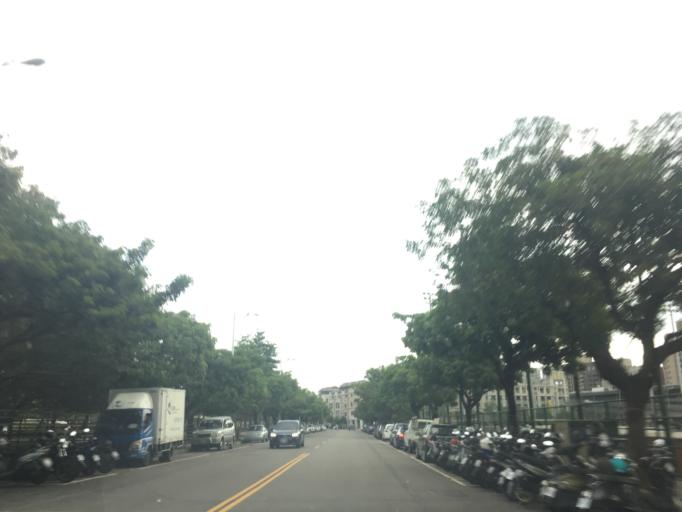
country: TW
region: Taiwan
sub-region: Taichung City
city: Taichung
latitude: 24.1611
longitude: 120.7205
